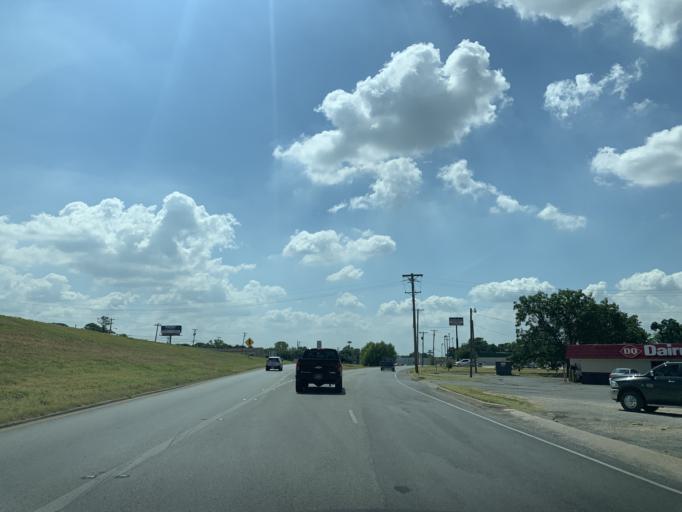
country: US
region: Texas
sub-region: Tarrant County
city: Azle
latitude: 32.8985
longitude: -97.5440
